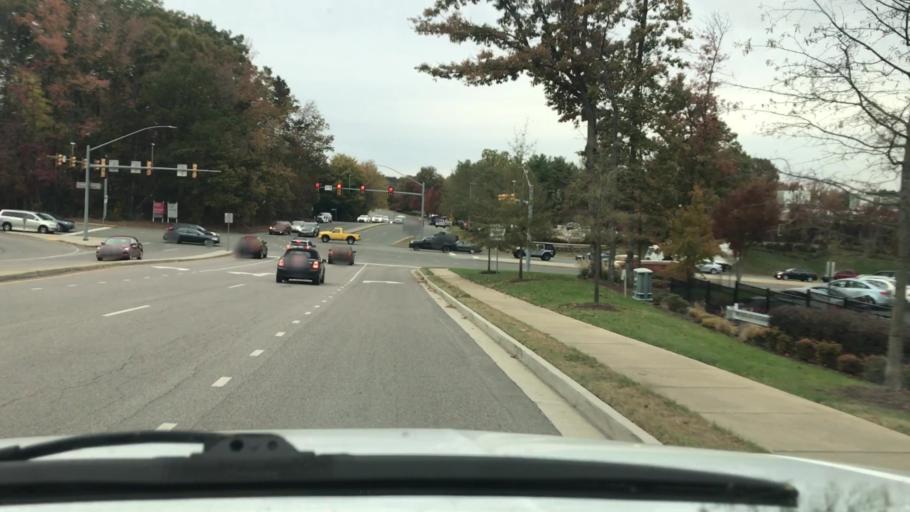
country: US
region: Virginia
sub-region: Henrico County
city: Tuckahoe
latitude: 37.6029
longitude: -77.5256
